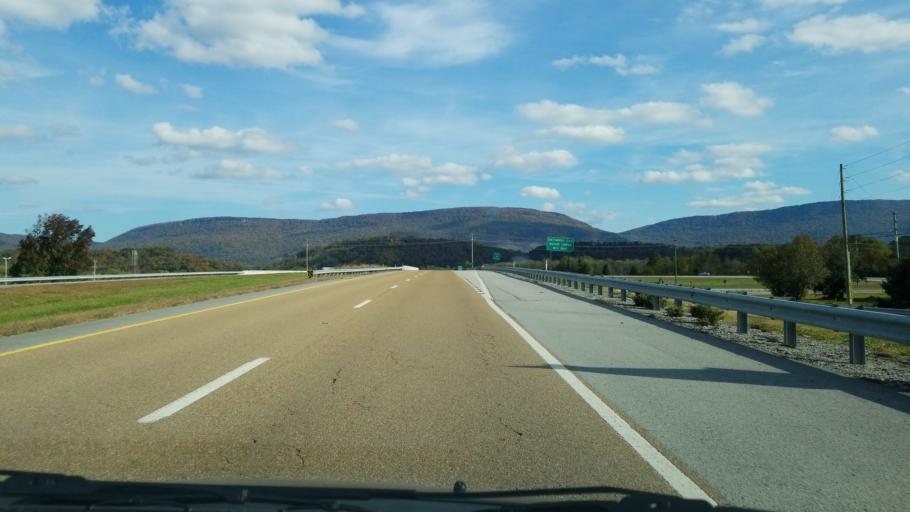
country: US
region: Tennessee
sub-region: Sequatchie County
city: Dunlap
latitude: 35.3961
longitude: -85.3760
